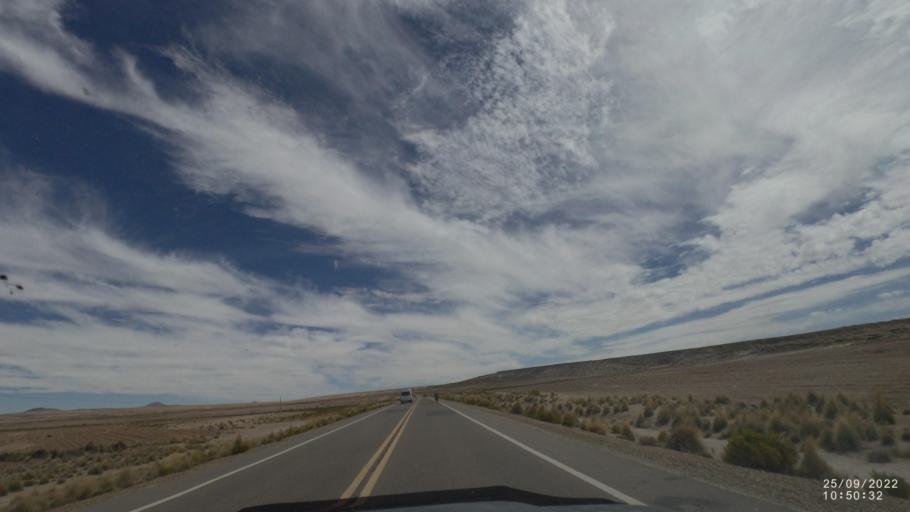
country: BO
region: Oruro
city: Challapata
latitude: -19.5746
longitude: -66.8386
